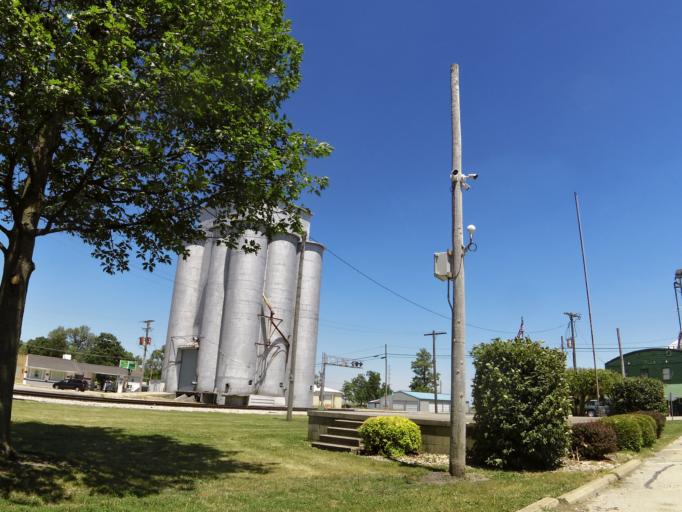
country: US
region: Illinois
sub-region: Livingston County
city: Chatsworth
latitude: 40.7582
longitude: -88.1909
